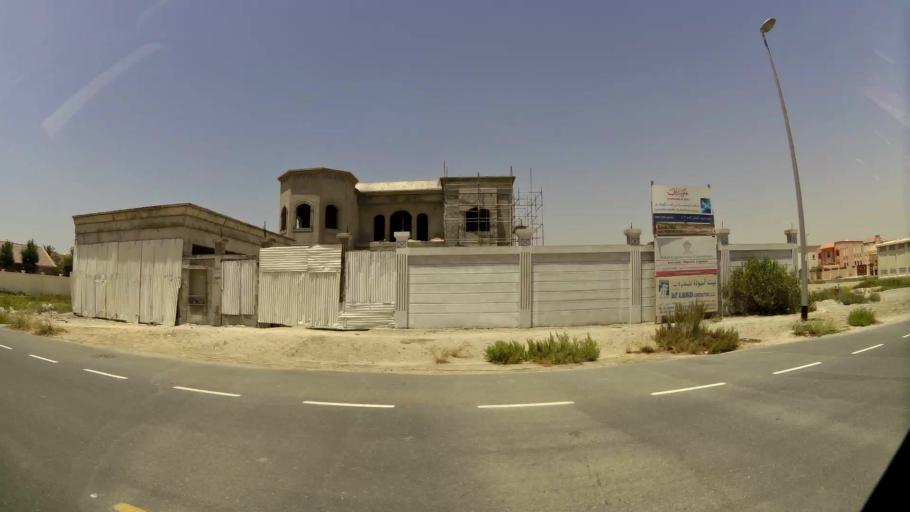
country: AE
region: Dubai
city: Dubai
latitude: 25.0844
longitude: 55.2029
